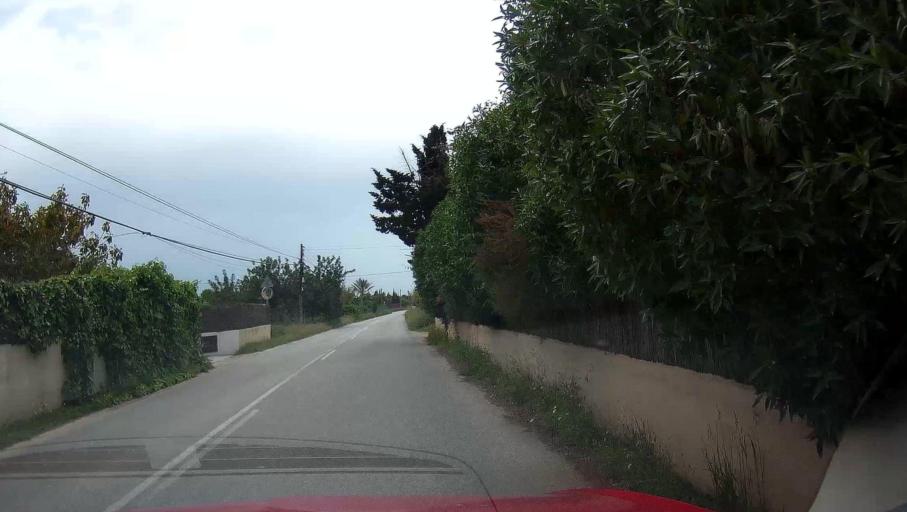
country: ES
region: Balearic Islands
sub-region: Illes Balears
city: Sant Josep de sa Talaia
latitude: 38.8755
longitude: 1.3548
